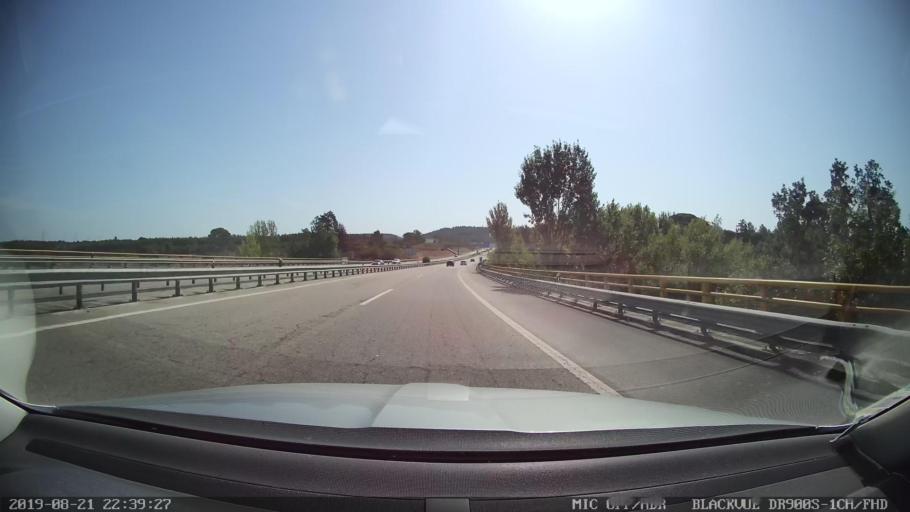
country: PT
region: Santarem
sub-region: Entroncamento
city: Entroncamento
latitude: 39.4892
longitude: -8.4570
